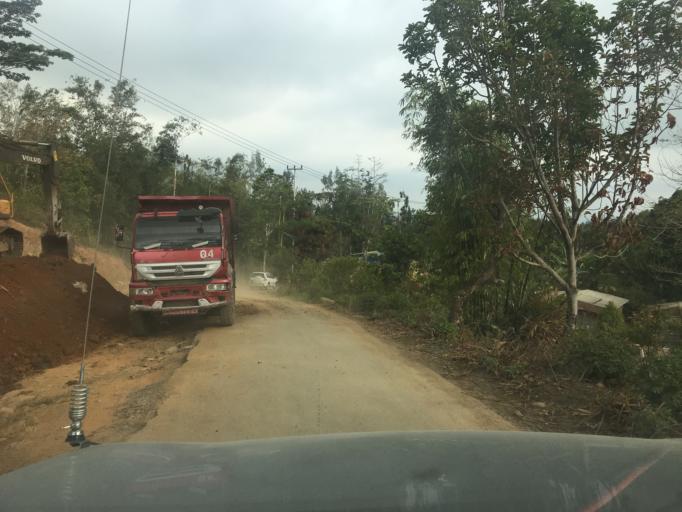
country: TL
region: Ainaro
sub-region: Ainaro
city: Ainaro
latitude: -9.0012
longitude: 125.4999
